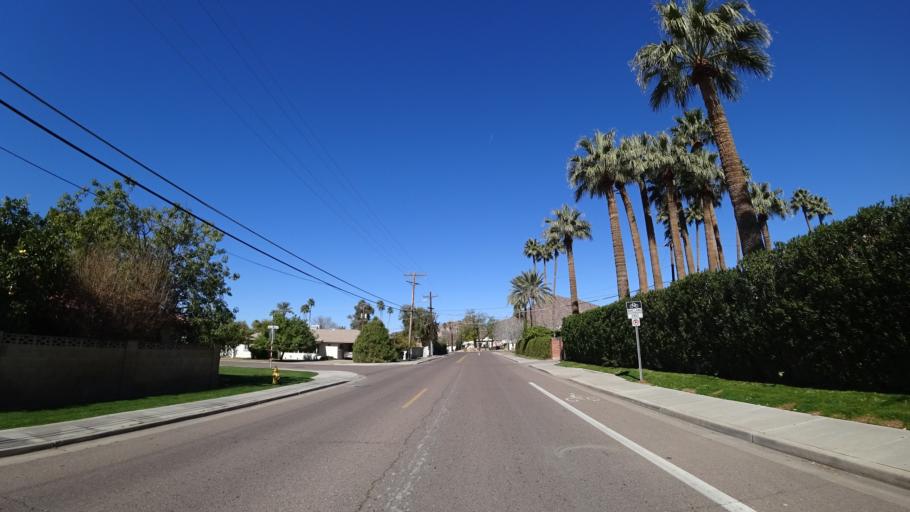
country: US
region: Arizona
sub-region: Maricopa County
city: Paradise Valley
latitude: 33.4863
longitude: -111.9695
